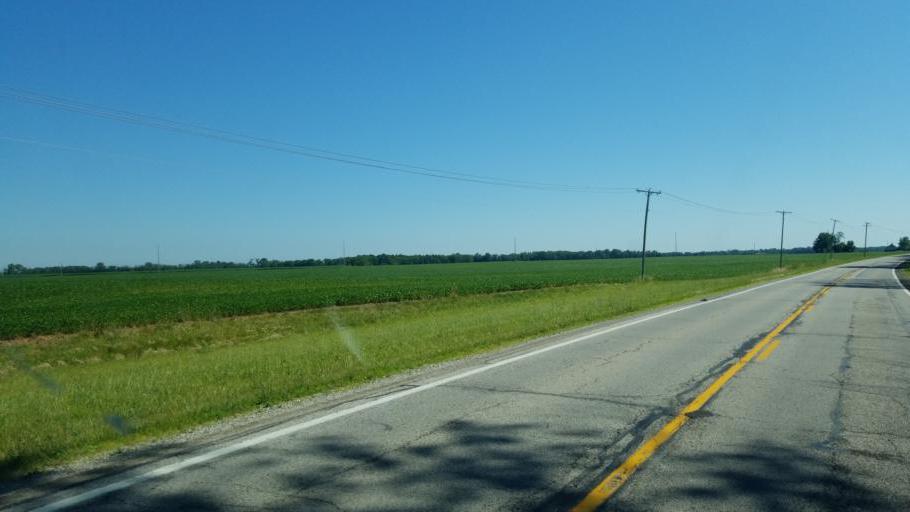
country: US
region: Ohio
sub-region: Marion County
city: Marion
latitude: 40.6837
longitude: -83.0970
